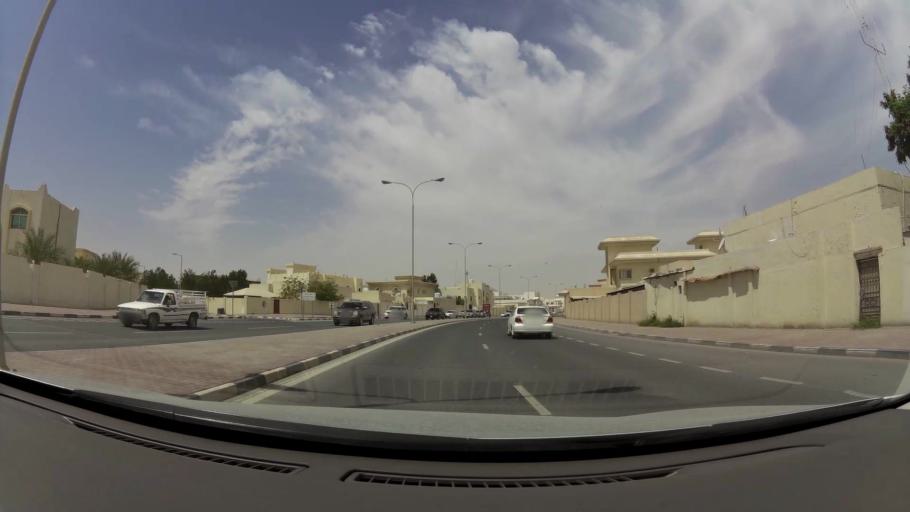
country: QA
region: Baladiyat ar Rayyan
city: Ar Rayyan
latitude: 25.2866
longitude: 51.4188
